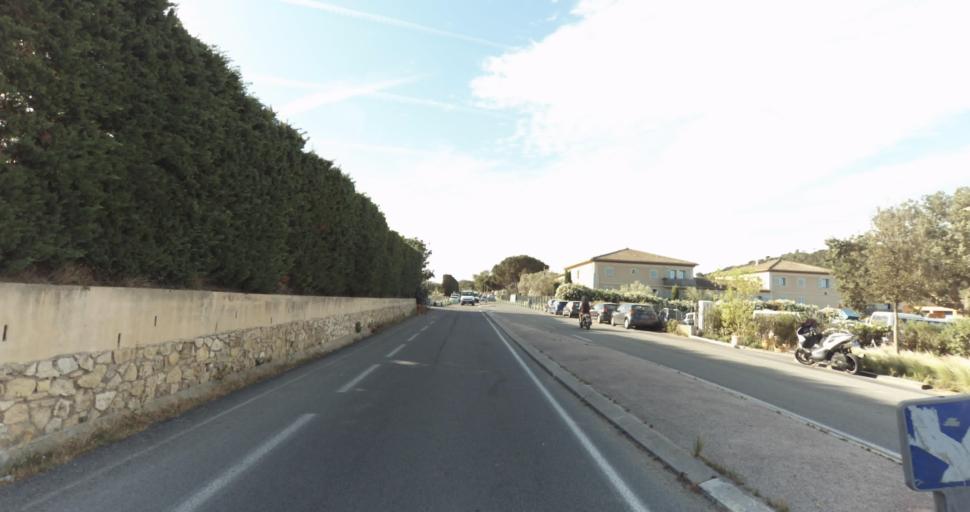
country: FR
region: Provence-Alpes-Cote d'Azur
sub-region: Departement du Var
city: Saint-Tropez
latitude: 43.2593
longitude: 6.6320
